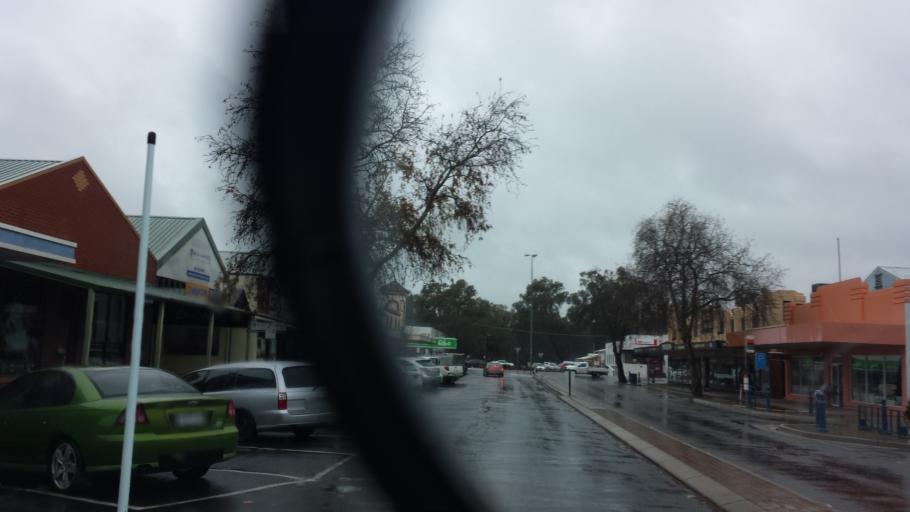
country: AU
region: Victoria
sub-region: Benalla
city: Benalla
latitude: -36.5501
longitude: 145.9855
